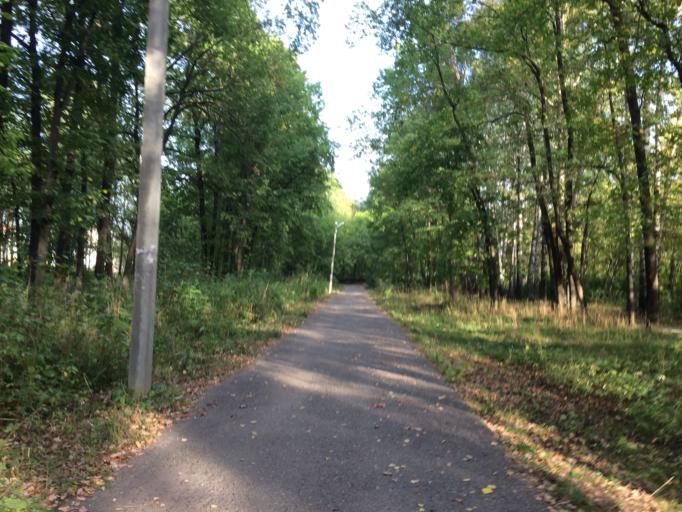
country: RU
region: Mariy-El
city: Medvedevo
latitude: 56.6269
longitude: 47.8174
